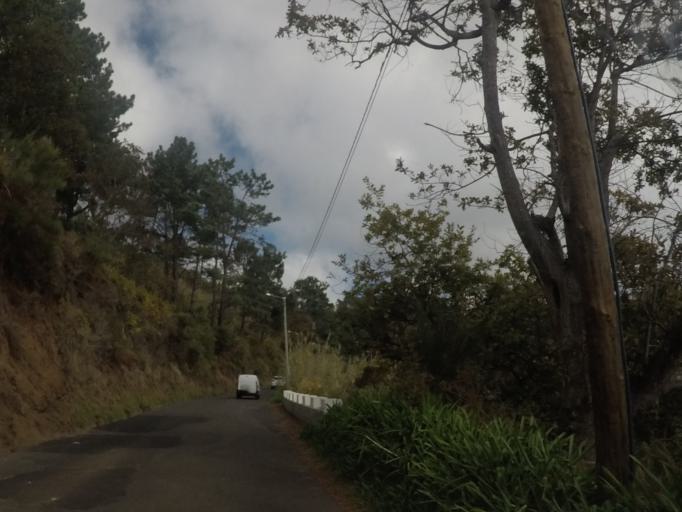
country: PT
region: Madeira
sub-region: Calheta
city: Faja da Ovelha
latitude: 32.7733
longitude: -17.2234
